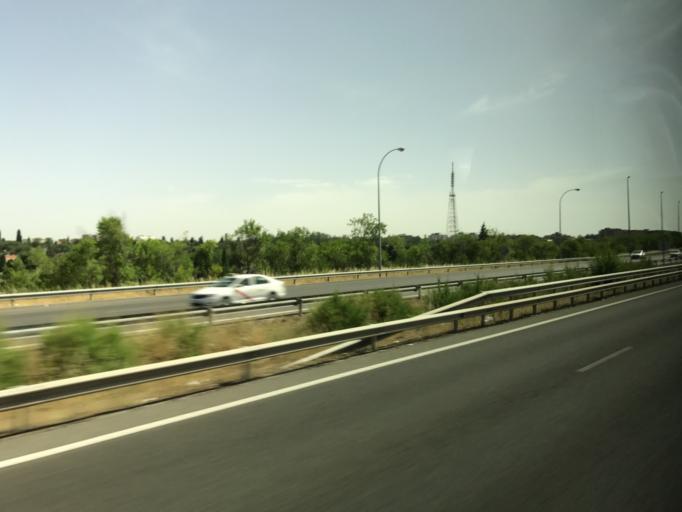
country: ES
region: Madrid
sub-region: Provincia de Madrid
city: Moratalaz
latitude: 40.4144
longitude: -3.6393
